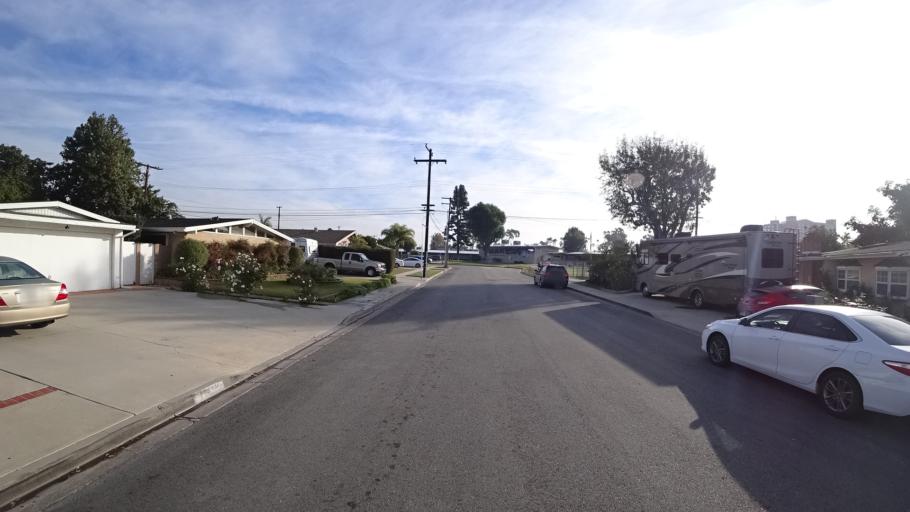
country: US
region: California
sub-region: Orange County
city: Garden Grove
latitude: 33.7938
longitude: -117.9198
